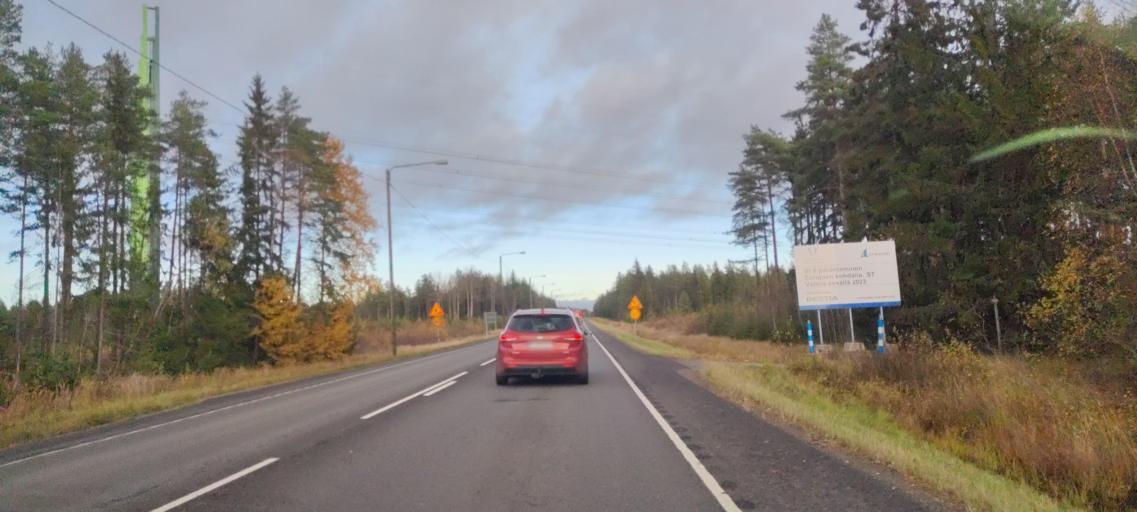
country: FI
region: Satakunta
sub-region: Rauma
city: Eurajoki
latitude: 61.1856
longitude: 21.6749
